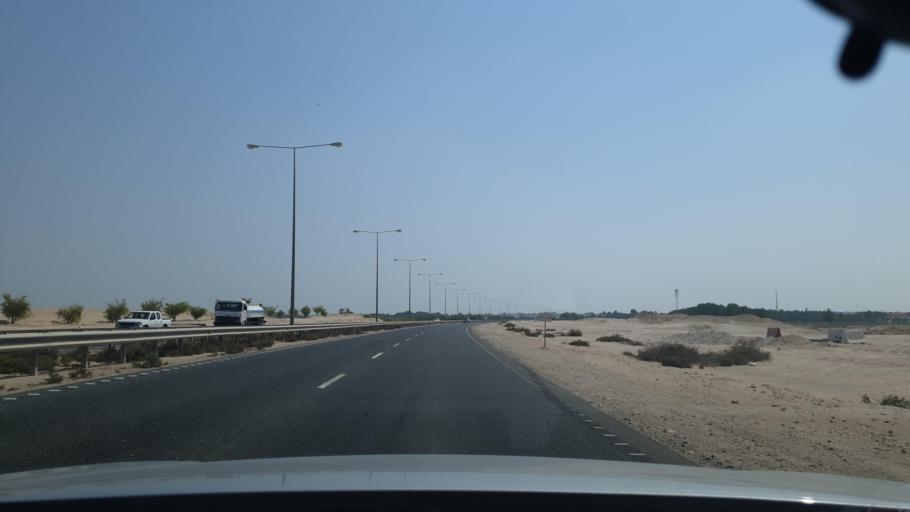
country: QA
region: Al Khawr
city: Al Khawr
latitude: 25.7366
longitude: 51.4914
